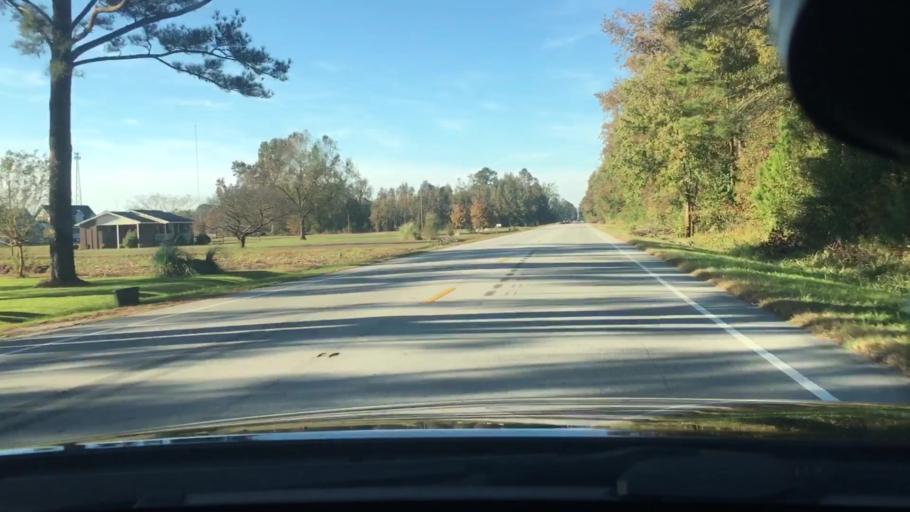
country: US
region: North Carolina
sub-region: Craven County
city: New Bern
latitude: 35.1700
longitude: -77.0427
